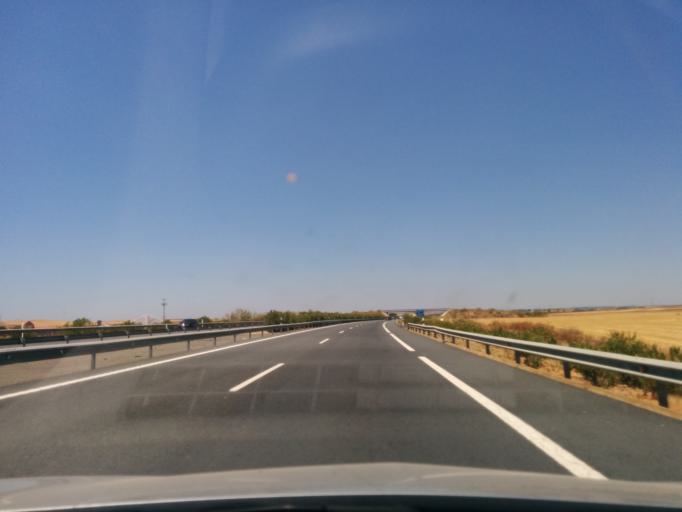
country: ES
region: Andalusia
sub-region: Provincia de Huelva
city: San Juan del Puerto
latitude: 37.3135
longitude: -6.8903
